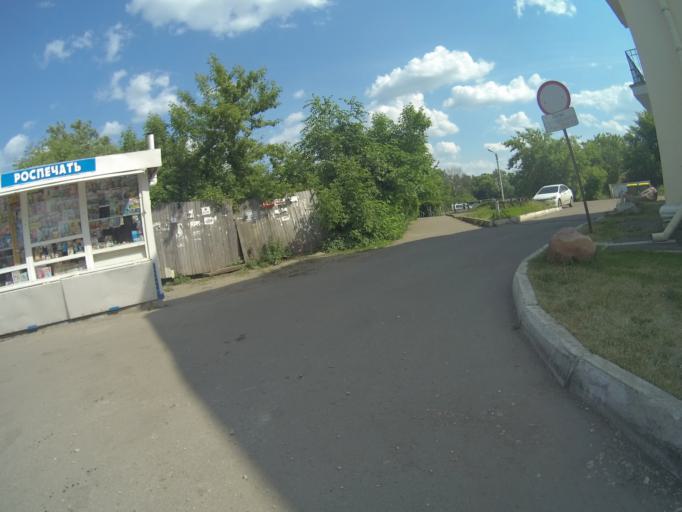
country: RU
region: Vladimir
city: Suzdal'
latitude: 56.4188
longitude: 40.4503
